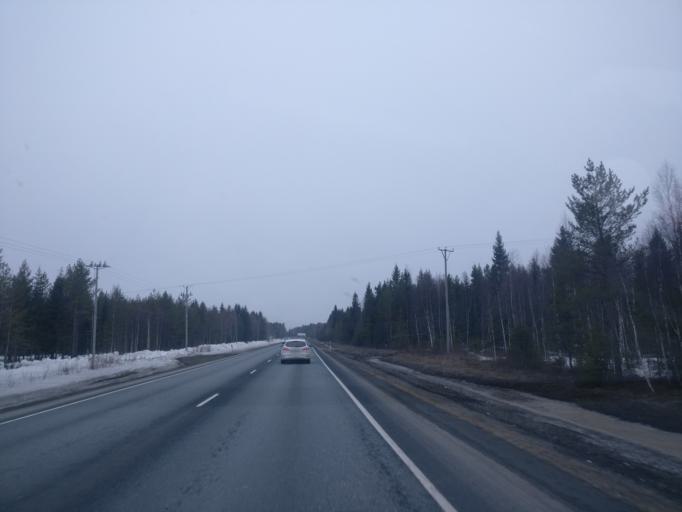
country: FI
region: Lapland
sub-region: Kemi-Tornio
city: Simo
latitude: 65.6719
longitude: 24.9135
